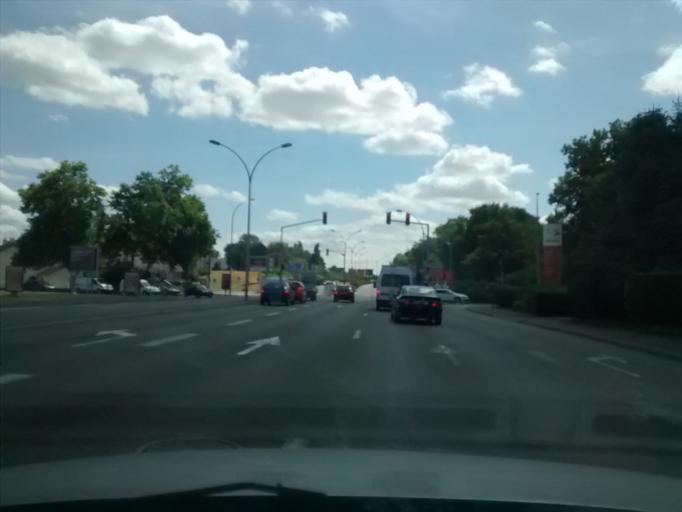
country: FR
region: Pays de la Loire
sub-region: Departement de la Sarthe
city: Le Mans
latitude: 47.9846
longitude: 0.1845
